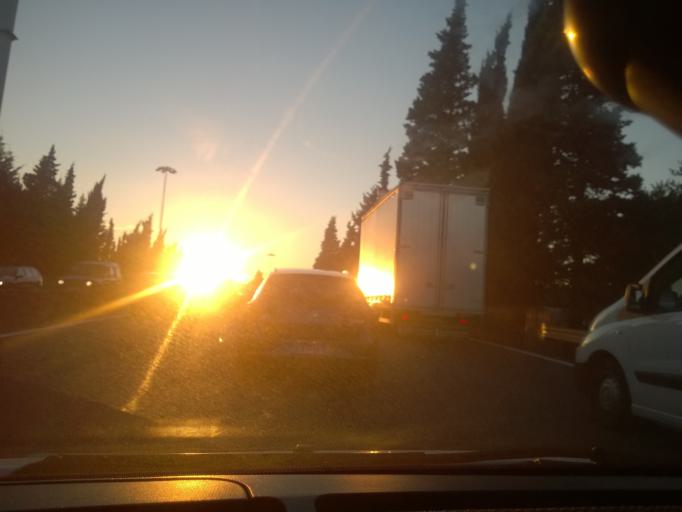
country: PT
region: Porto
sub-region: Porto
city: Porto
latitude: 41.1744
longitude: -8.6112
